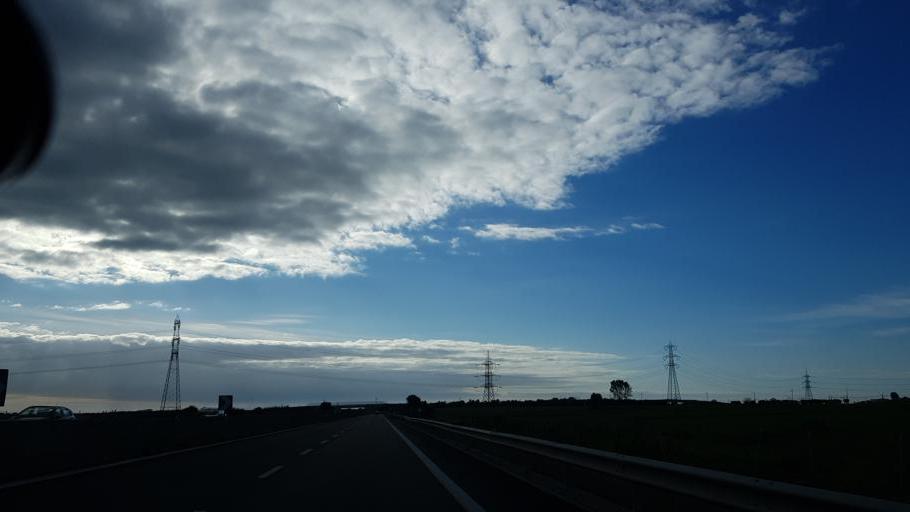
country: IT
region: Apulia
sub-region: Provincia di Brindisi
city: La Rosa
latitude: 40.6051
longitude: 17.9645
